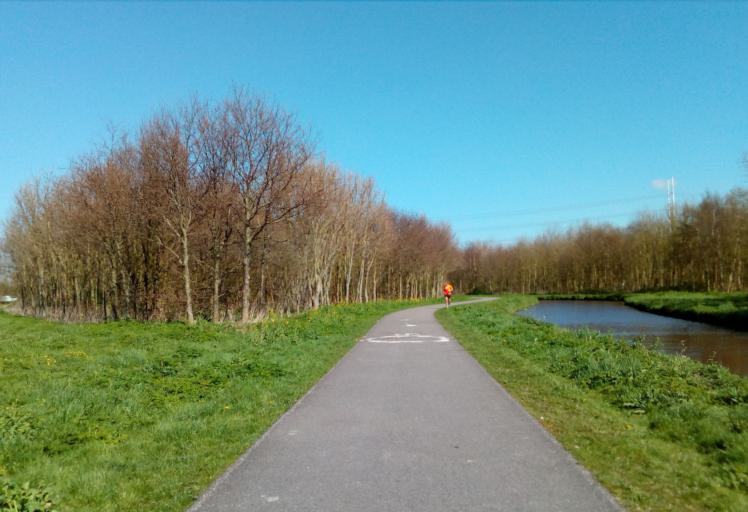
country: NL
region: South Holland
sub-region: Gemeente Rijswijk
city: Rijswijk
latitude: 52.0053
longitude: 4.3058
